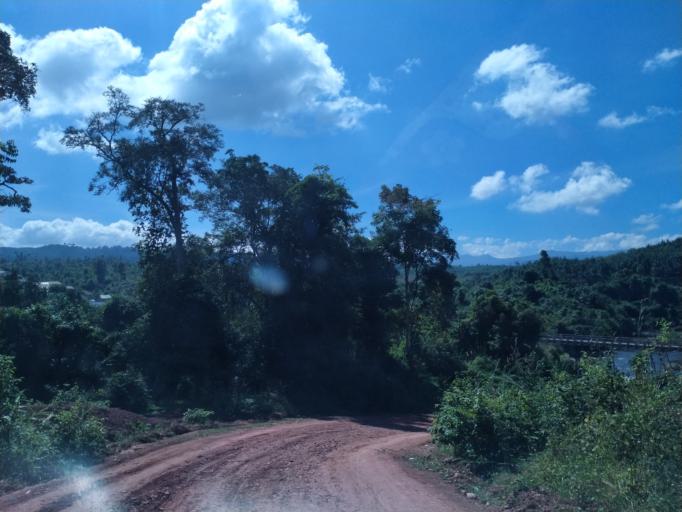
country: LA
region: Vientiane
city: Muang Phon-Hong
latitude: 18.6107
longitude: 102.8496
